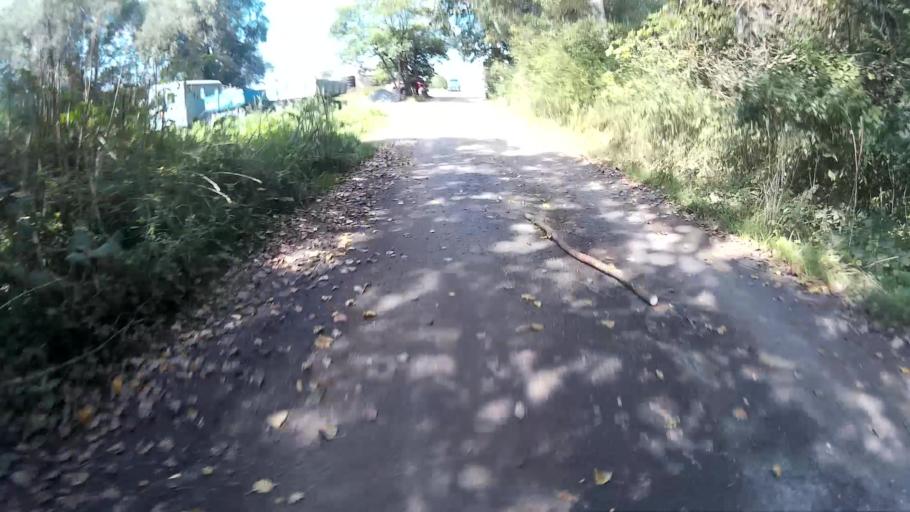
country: CZ
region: South Moravian
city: Hrusovany nad Jevisovkou
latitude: 48.7941
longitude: 16.4315
